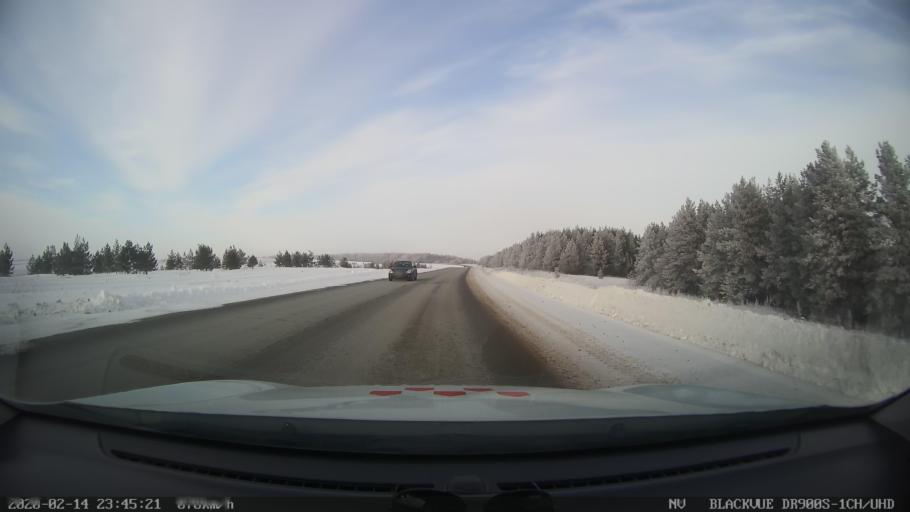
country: RU
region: Tatarstan
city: Kuybyshevskiy Zaton
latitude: 55.2197
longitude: 49.2318
